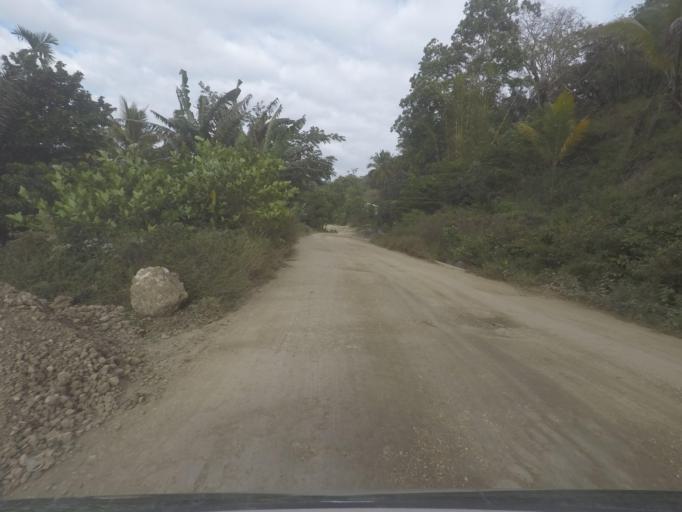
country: TL
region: Baucau
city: Venilale
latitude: -8.6033
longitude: 126.3832
